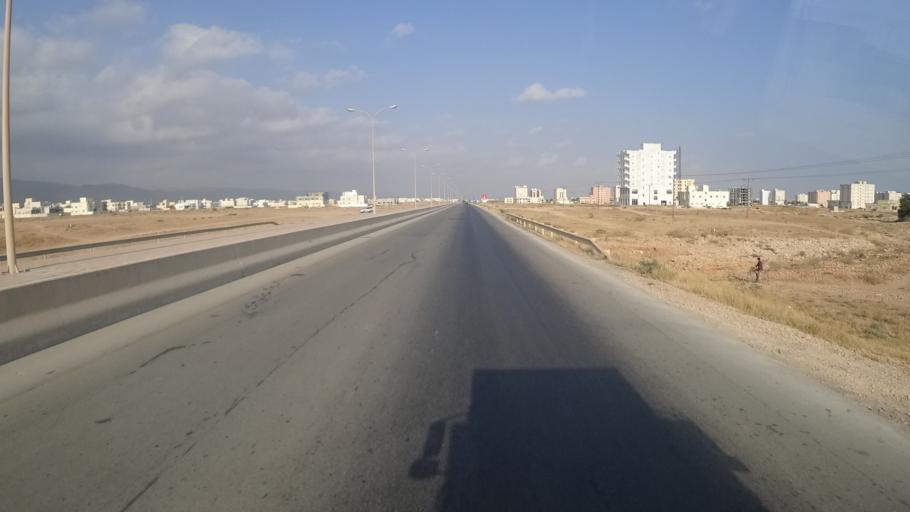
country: OM
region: Zufar
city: Salalah
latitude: 17.0250
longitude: 54.0205
